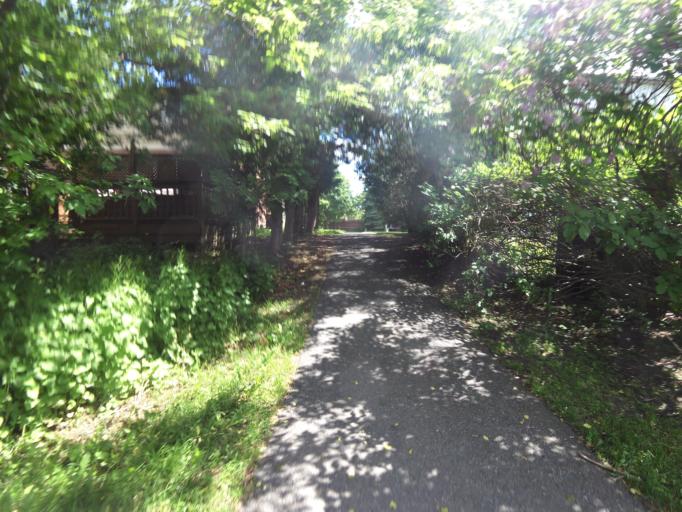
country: CA
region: Ontario
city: Ottawa
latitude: 45.3602
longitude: -75.6363
